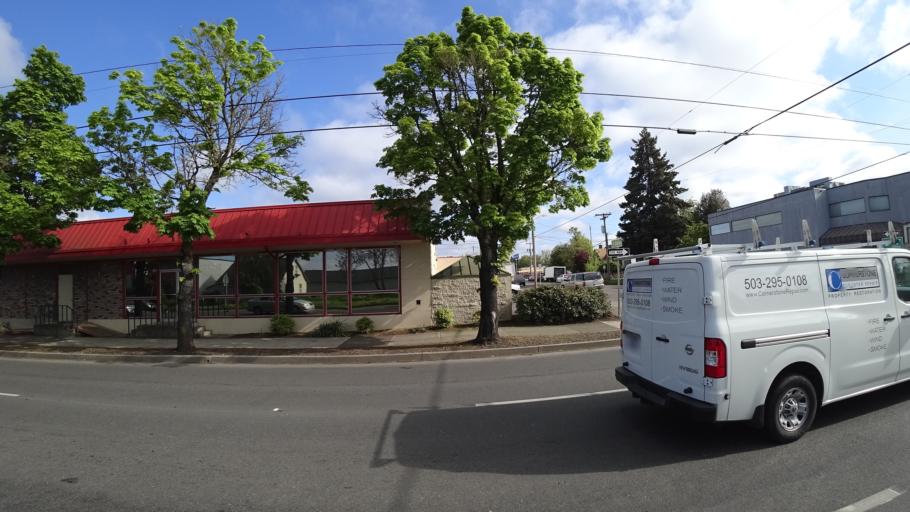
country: US
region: Oregon
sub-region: Washington County
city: Hillsboro
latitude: 45.5189
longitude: -122.9885
